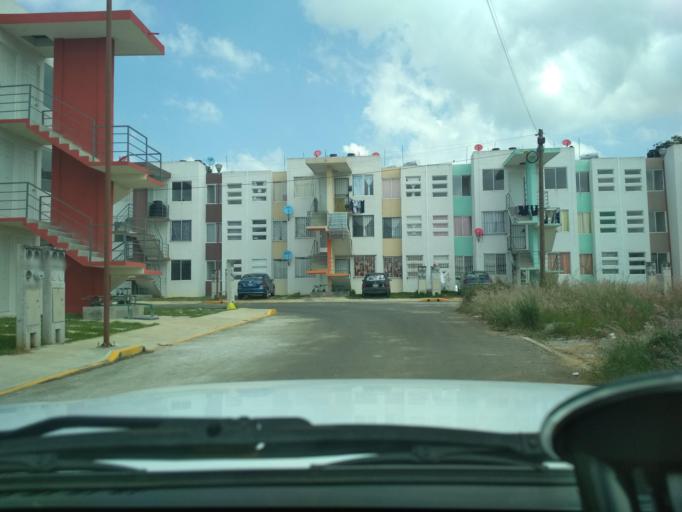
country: MX
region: Veracruz
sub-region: Fortin
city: Fraccionamiento los Alamos
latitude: 18.9316
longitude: -96.9754
